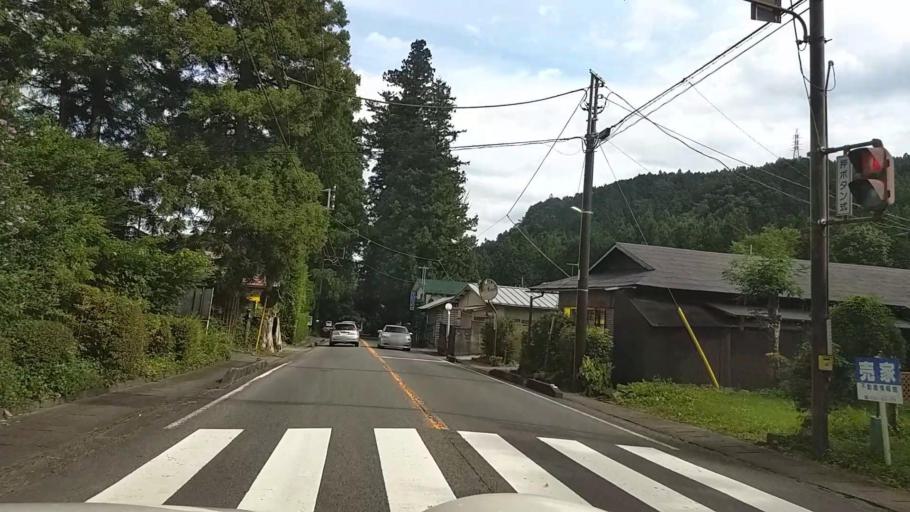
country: JP
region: Tochigi
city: Nikko
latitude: 36.7423
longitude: 139.6302
